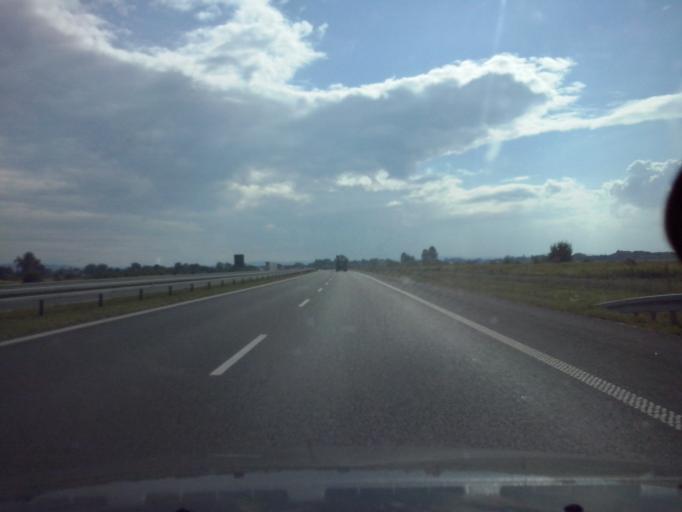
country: PL
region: Lesser Poland Voivodeship
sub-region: Powiat tarnowski
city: Wierzchoslawice
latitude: 50.0357
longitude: 20.8830
